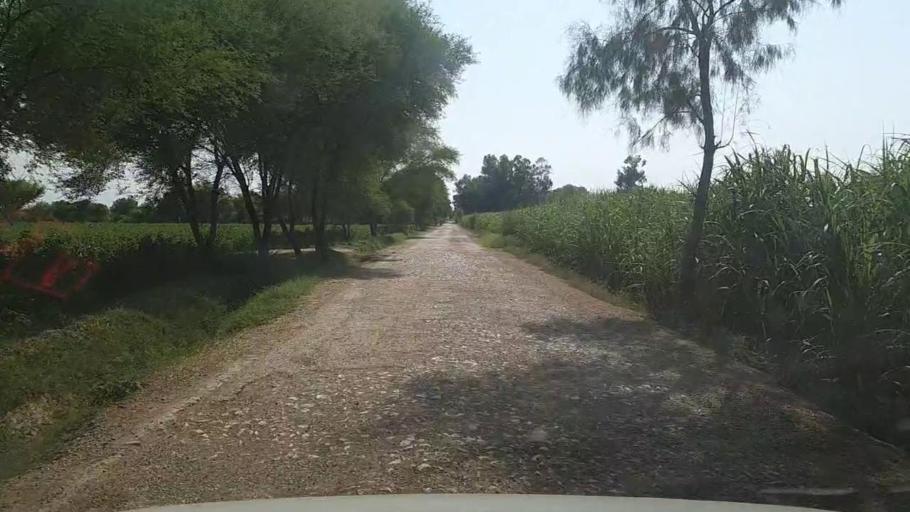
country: PK
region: Sindh
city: Mirpur Mathelo
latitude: 28.1203
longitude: 69.6003
